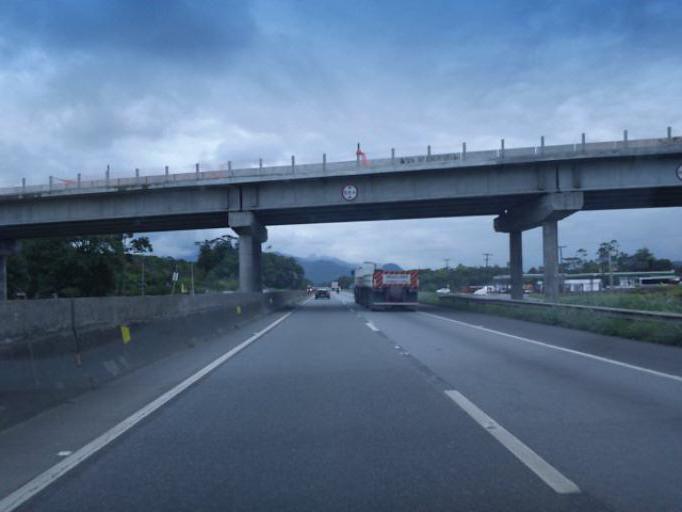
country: BR
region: Santa Catarina
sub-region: Joinville
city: Joinville
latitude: -26.0664
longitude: -48.8604
